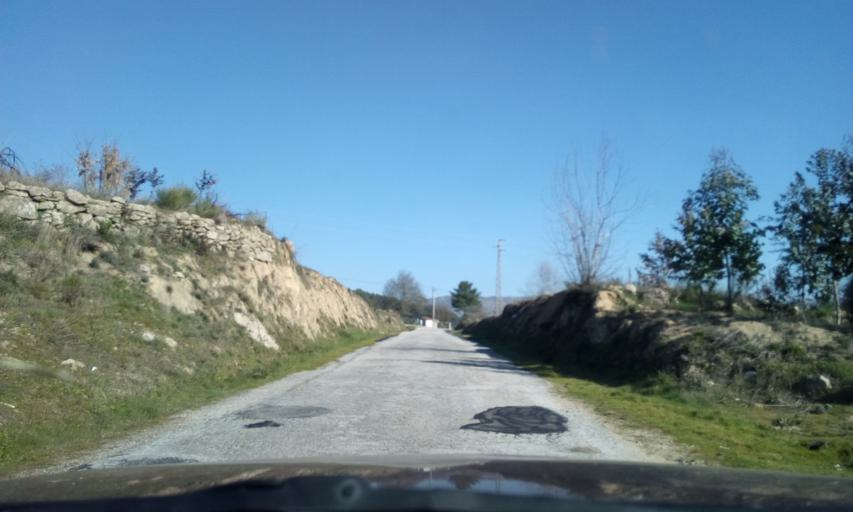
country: PT
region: Guarda
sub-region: Celorico da Beira
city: Celorico da Beira
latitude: 40.6852
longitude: -7.4551
